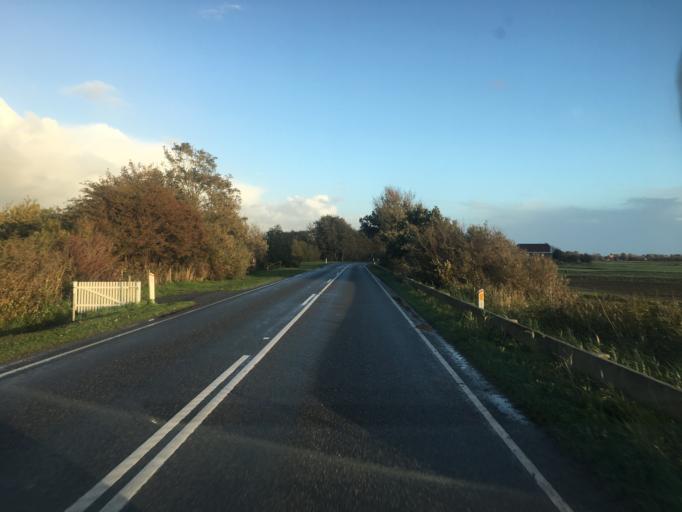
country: DE
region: Schleswig-Holstein
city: Neukirchen
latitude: 54.9148
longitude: 8.7384
